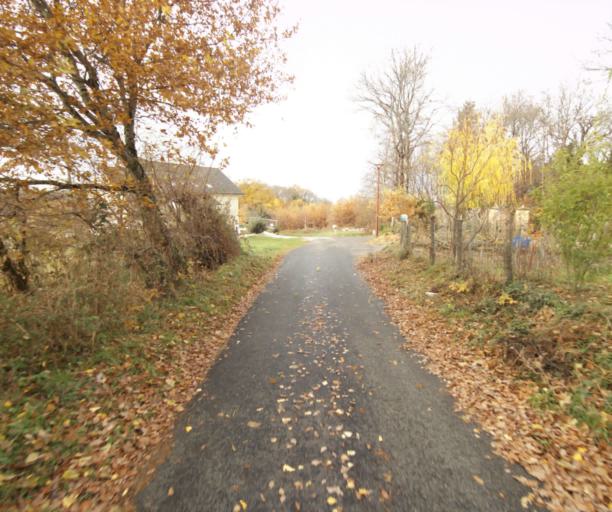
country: FR
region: Limousin
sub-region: Departement de la Correze
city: Beynat
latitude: 45.1738
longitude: 1.7311
